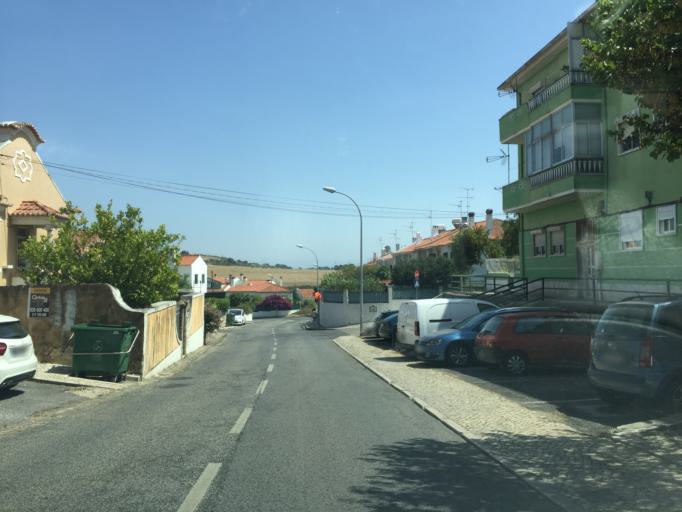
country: PT
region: Lisbon
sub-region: Oeiras
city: Barcarena
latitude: 38.7445
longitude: -9.2838
